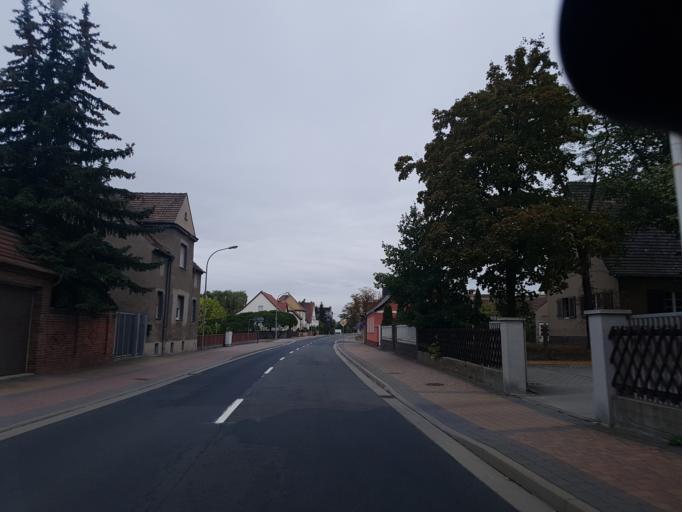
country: DE
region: Saxony-Anhalt
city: Prettin
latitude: 51.6628
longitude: 12.9223
